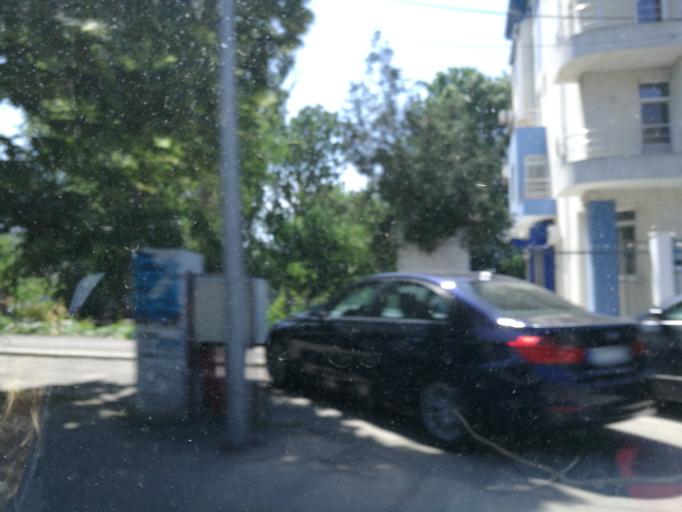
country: RO
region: Constanta
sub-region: Municipiul Constanta
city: Constanta
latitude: 44.2082
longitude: 28.6432
